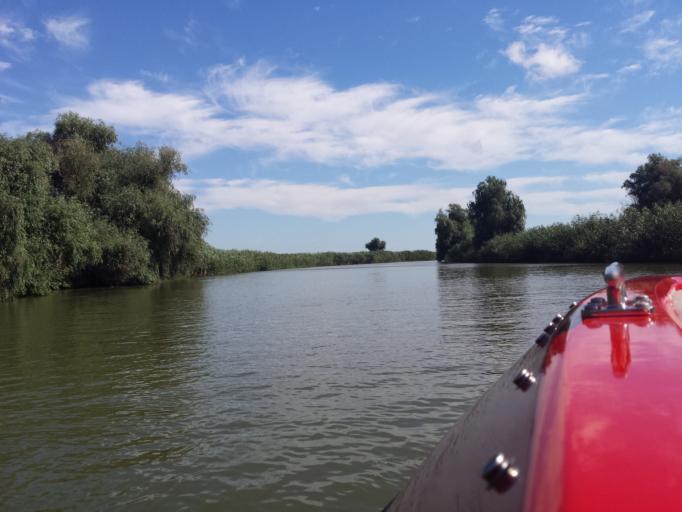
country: RO
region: Tulcea
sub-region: Comuna Crisan
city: Crisan
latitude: 45.2150
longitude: 29.2149
